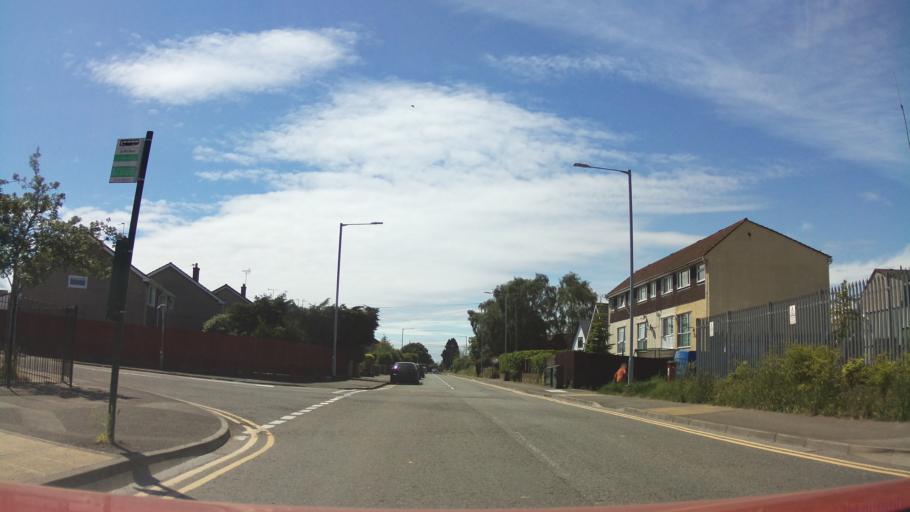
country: GB
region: Wales
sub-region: Monmouthshire
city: Caldicot
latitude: 51.5890
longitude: -2.7538
